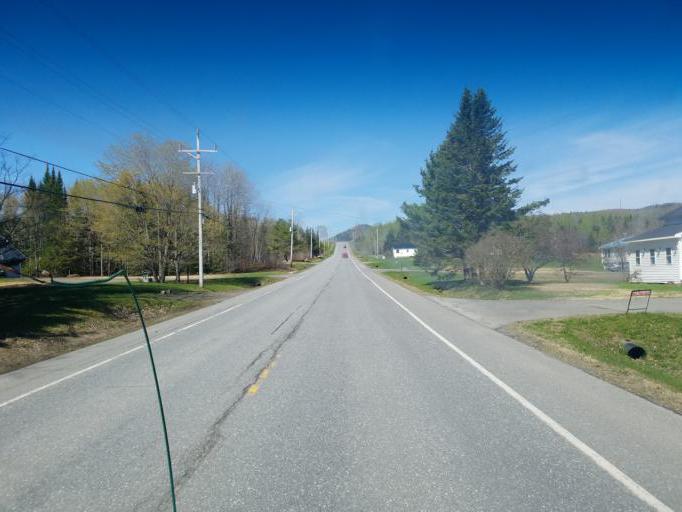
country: US
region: Maine
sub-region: Aroostook County
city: Presque Isle
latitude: 46.6668
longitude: -68.2048
